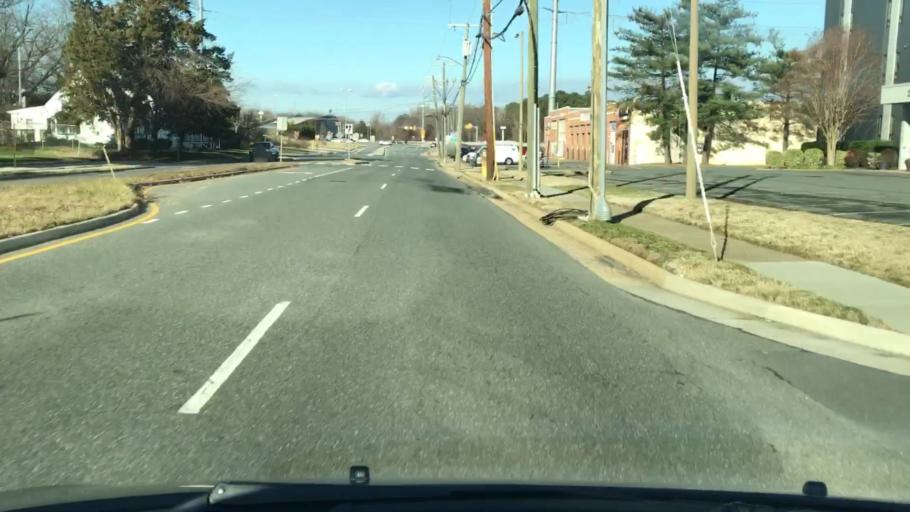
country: US
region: Virginia
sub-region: Fairfax County
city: Huntington
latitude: 38.7971
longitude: -77.0769
